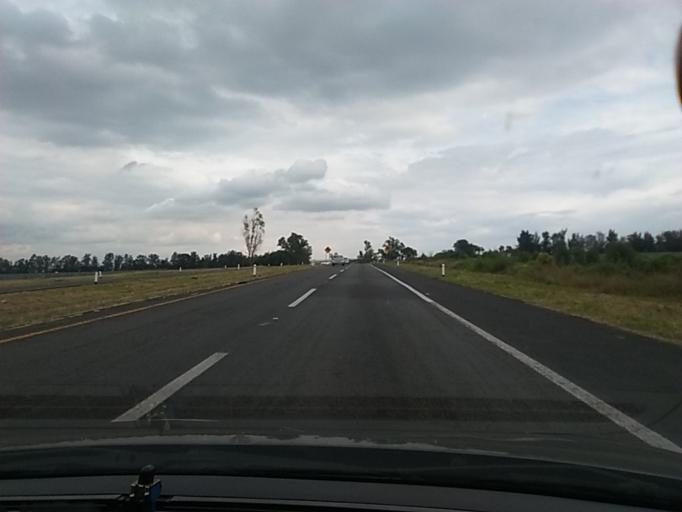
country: MX
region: Jalisco
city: Ocotlan
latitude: 20.3846
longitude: -102.7069
